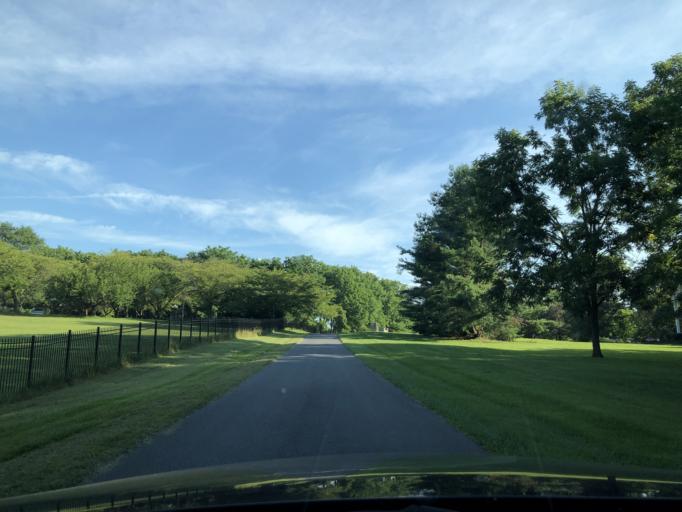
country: US
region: Maryland
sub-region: Howard County
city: Highland
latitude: 39.1903
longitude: -76.9377
